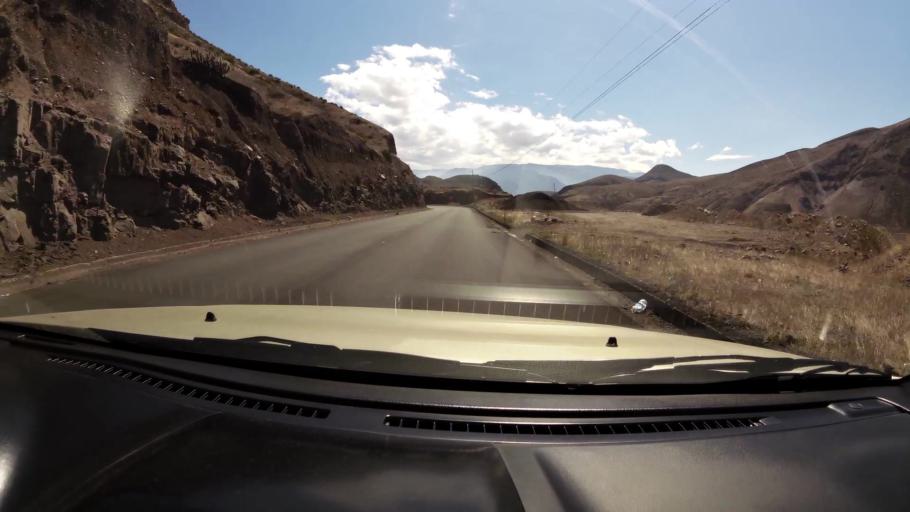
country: EC
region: El Oro
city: Zaruma
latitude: -3.3450
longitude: -79.3959
